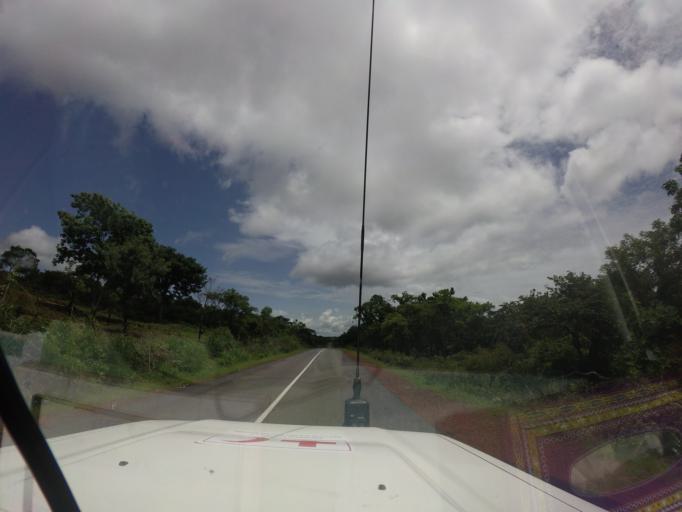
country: GN
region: Faranah
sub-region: Faranah Prefecture
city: Faranah
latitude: 10.0213
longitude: -10.8127
